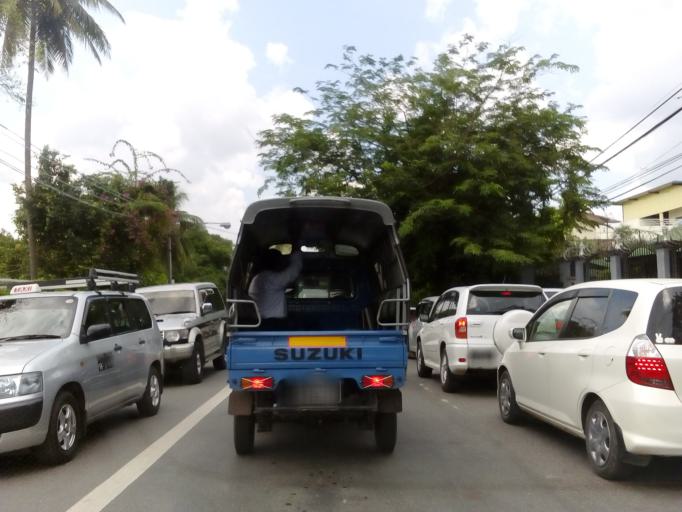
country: MM
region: Yangon
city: Yangon
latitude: 16.8194
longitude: 96.1590
